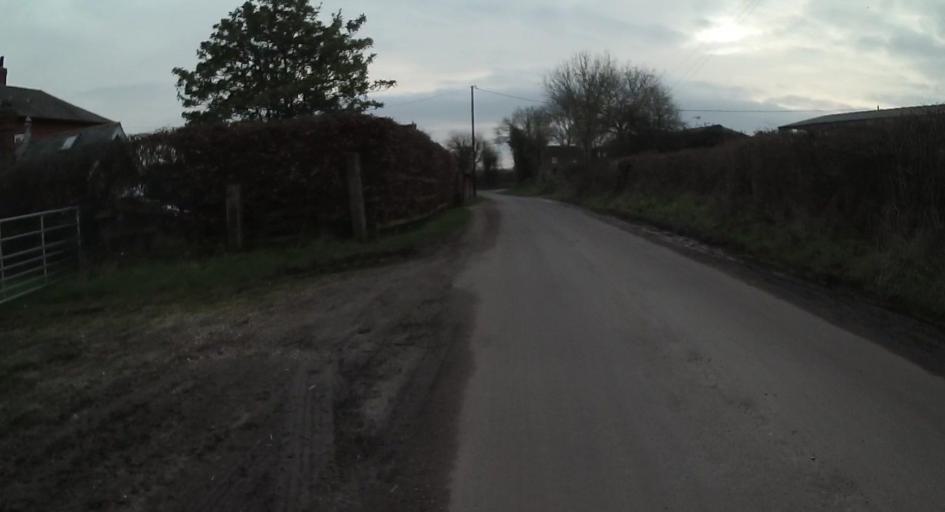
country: GB
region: England
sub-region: West Berkshire
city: Stratfield Mortimer
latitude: 51.3616
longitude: -1.0626
